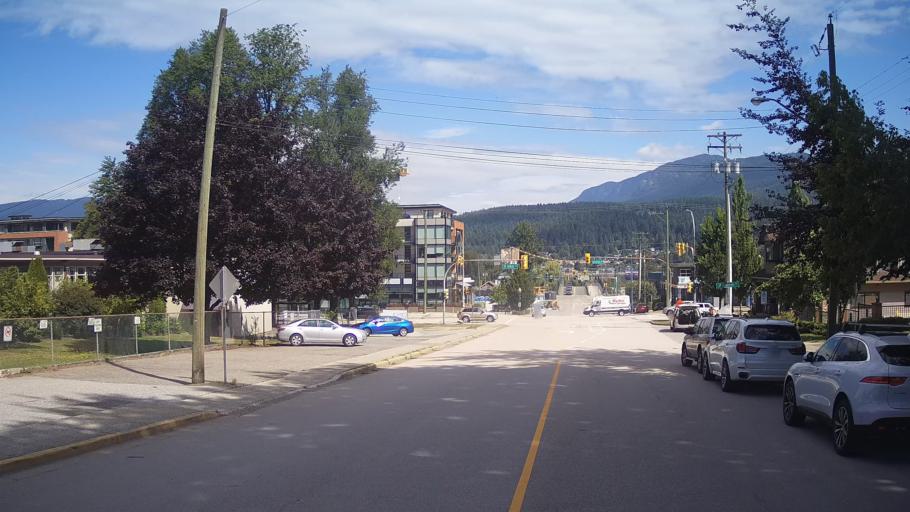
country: CA
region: British Columbia
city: Port Moody
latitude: 49.2759
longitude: -122.8502
